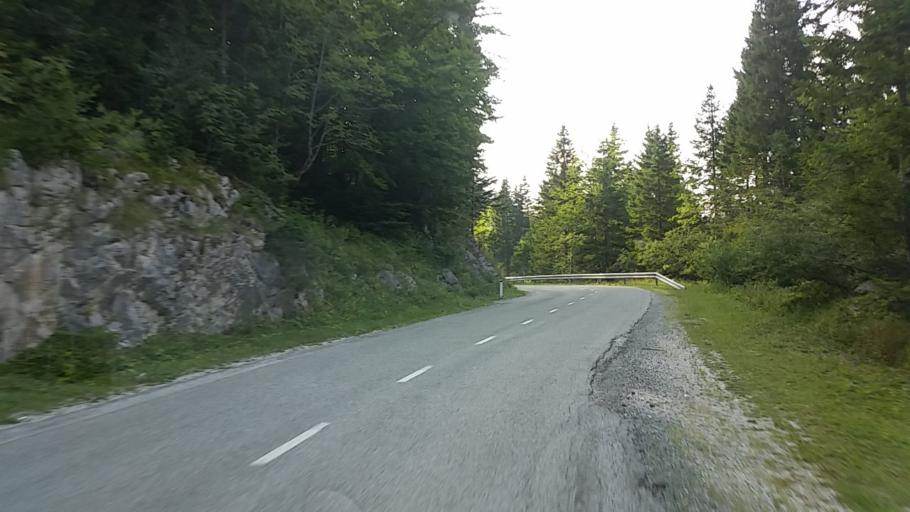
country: SI
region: Bohinj
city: Bohinjska Bistrica
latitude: 46.2388
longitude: 14.0142
